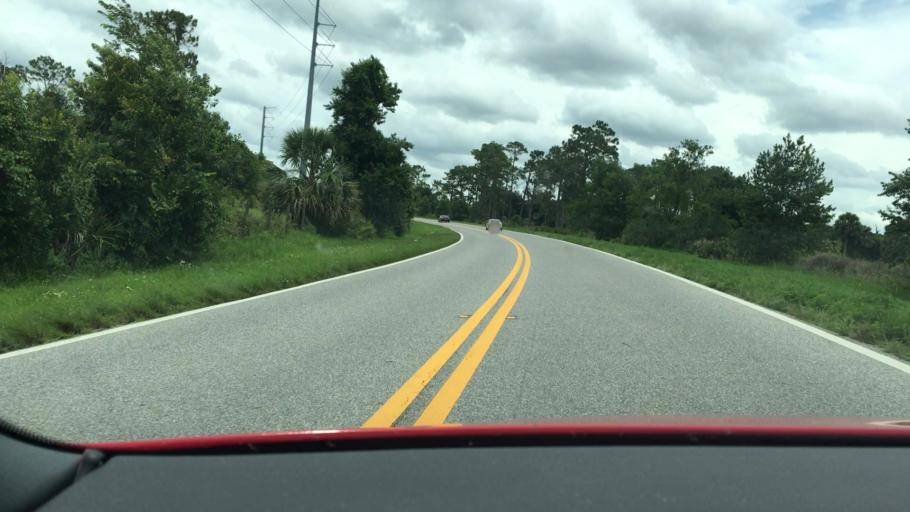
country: US
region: Florida
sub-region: Lake County
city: Eustis
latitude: 28.8699
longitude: -81.6612
